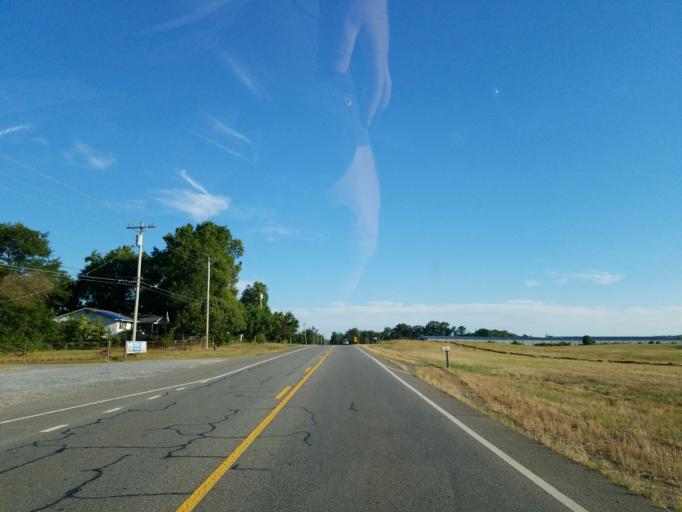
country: US
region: Georgia
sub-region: Gordon County
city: Calhoun
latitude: 34.4484
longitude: -84.9355
